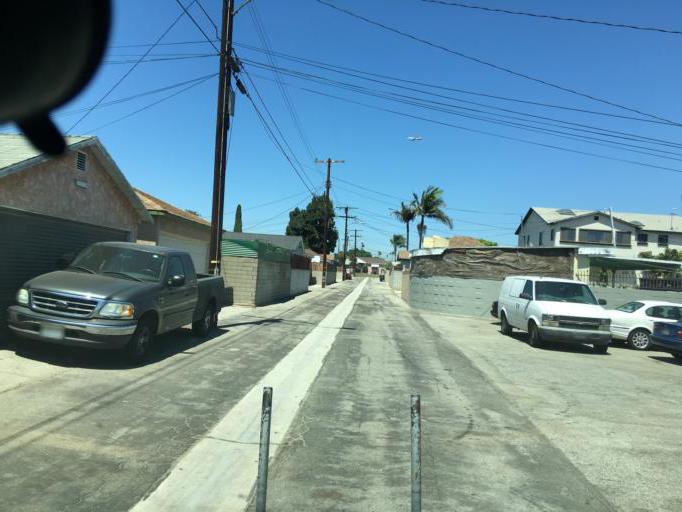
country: US
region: California
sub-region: Los Angeles County
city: West Athens
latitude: 33.9321
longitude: -118.3172
